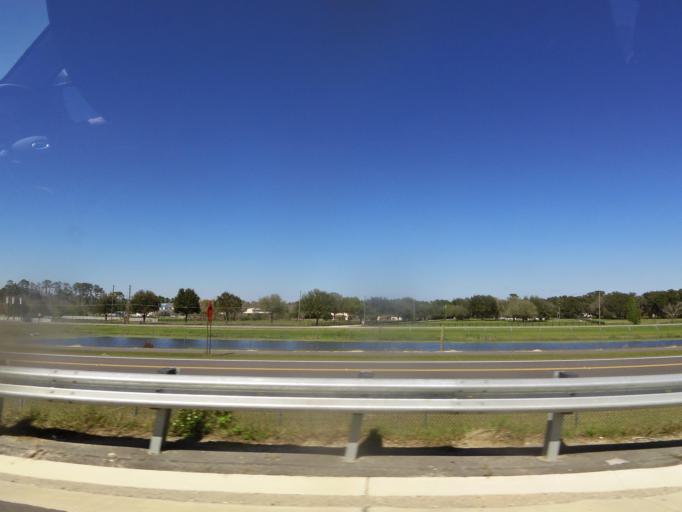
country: US
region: Florida
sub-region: Seminole County
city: Heathrow
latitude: 28.8133
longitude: -81.4354
